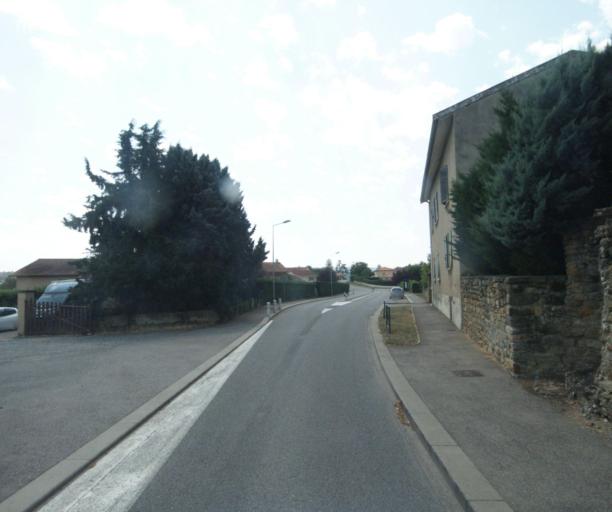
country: FR
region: Rhone-Alpes
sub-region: Departement du Rhone
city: Saint-Germain-Nuelles
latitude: 45.8484
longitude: 4.6219
